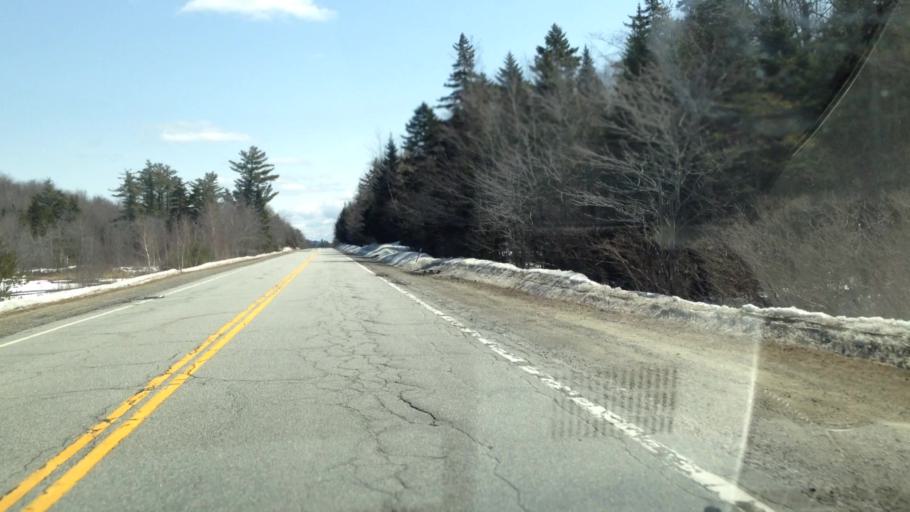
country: US
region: New Hampshire
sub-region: Sullivan County
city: Springfield
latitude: 43.4969
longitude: -72.0080
